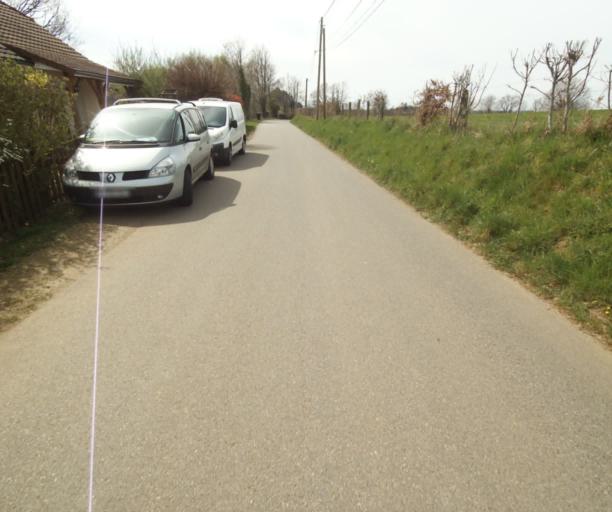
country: FR
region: Limousin
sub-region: Departement de la Correze
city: Naves
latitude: 45.3057
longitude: 1.7667
